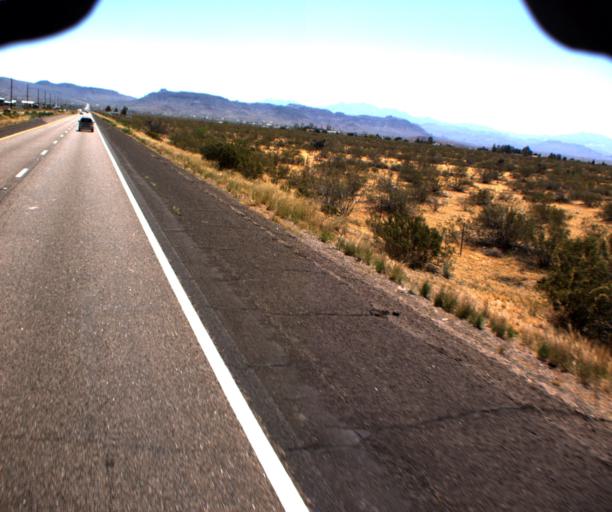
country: US
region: Arizona
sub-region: Mohave County
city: Golden Valley
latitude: 35.2224
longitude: -114.2261
